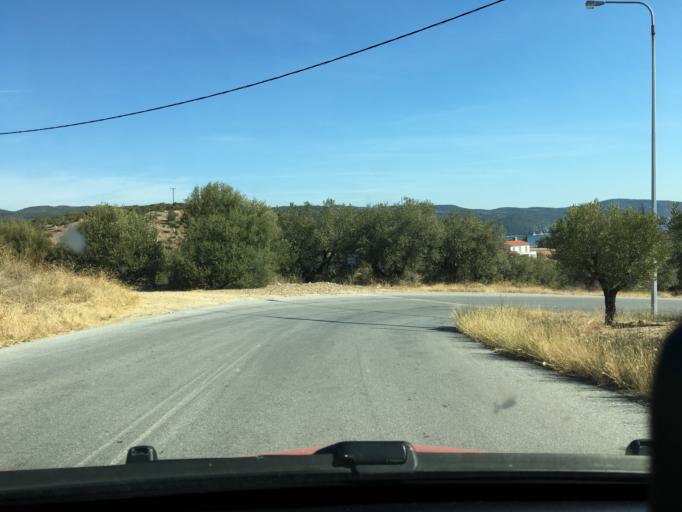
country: GR
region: Central Macedonia
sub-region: Nomos Chalkidikis
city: Agios Nikolaos
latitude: 40.3432
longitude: 23.7217
